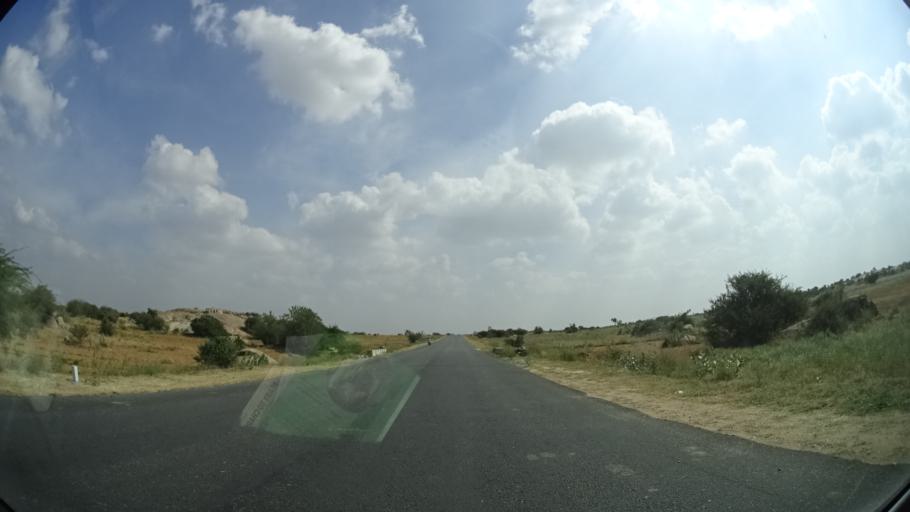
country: IN
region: Andhra Pradesh
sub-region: Anantapur
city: Uravakonda
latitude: 14.8185
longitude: 77.3430
